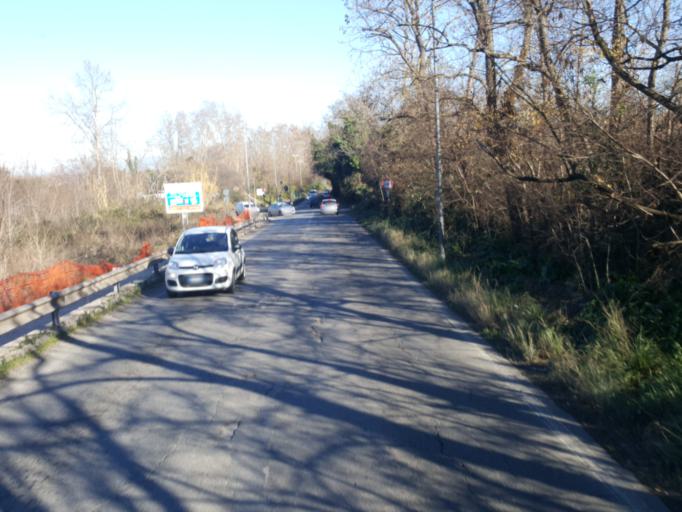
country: IT
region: Latium
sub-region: Citta metropolitana di Roma Capitale
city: Vitinia
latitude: 41.7901
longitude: 12.3786
